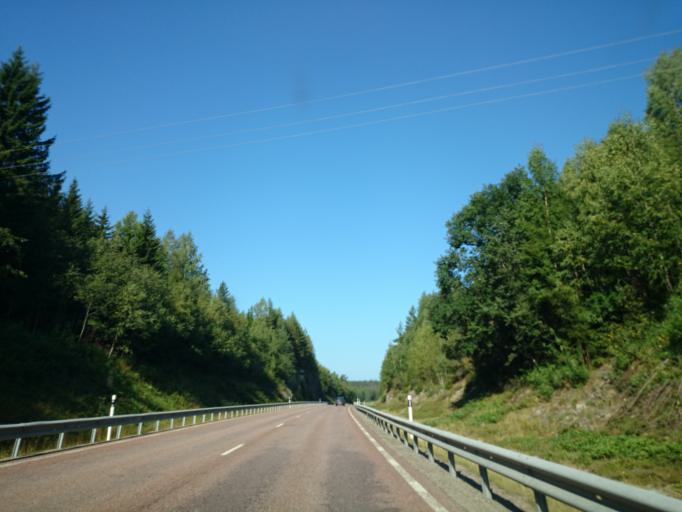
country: SE
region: Gaevleborg
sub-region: Hudiksvalls Kommun
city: Sorforsa
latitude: 61.7405
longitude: 16.8672
